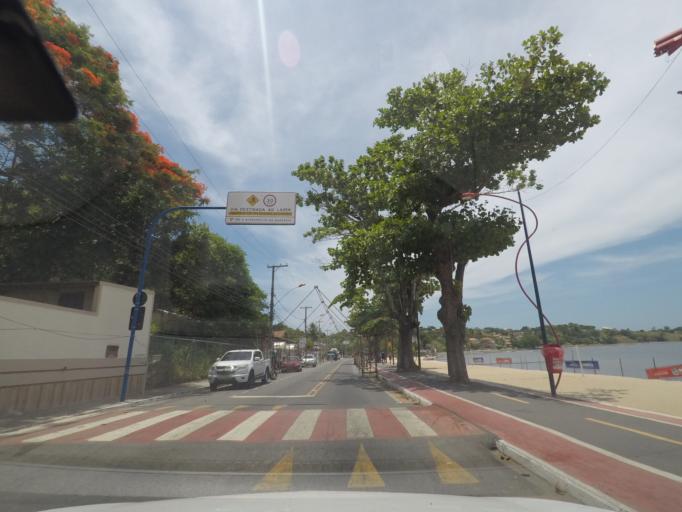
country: BR
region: Rio de Janeiro
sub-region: Marica
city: Marica
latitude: -22.9257
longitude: -42.8277
